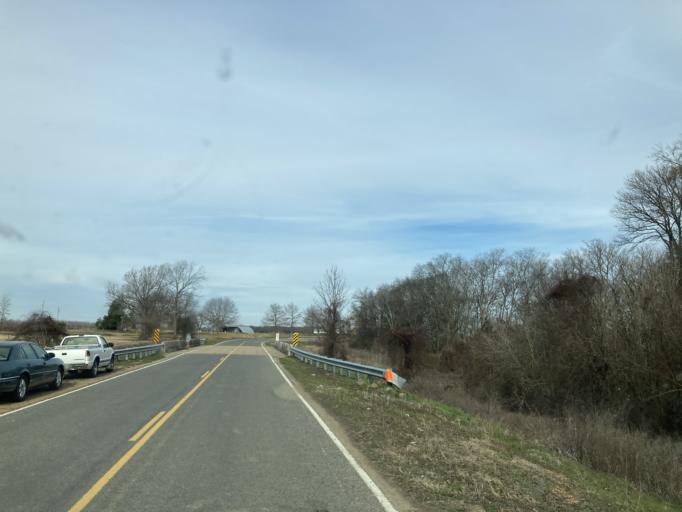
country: US
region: Mississippi
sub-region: Humphreys County
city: Belzoni
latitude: 33.1223
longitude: -90.6144
